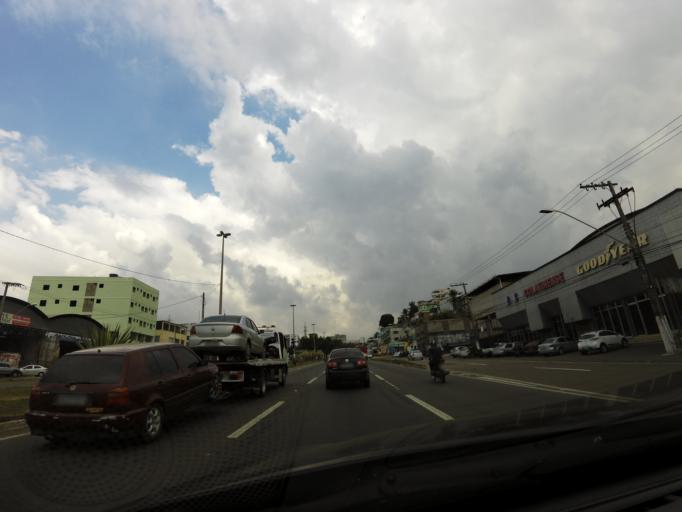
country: BR
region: Espirito Santo
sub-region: Vitoria
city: Vitoria
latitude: -20.3346
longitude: -40.3708
